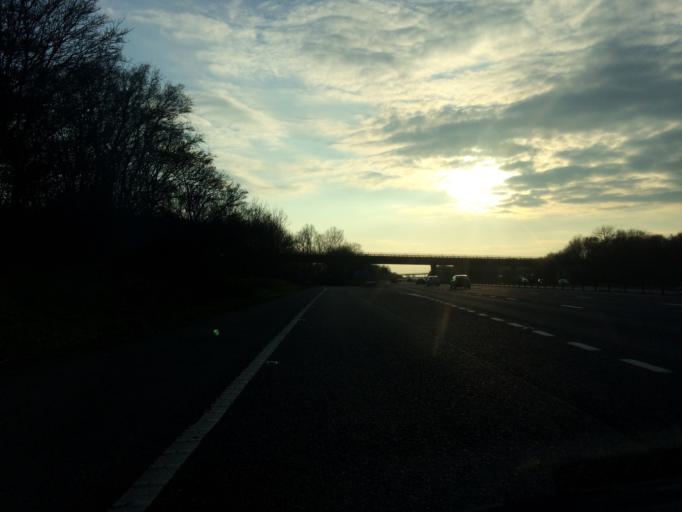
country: GB
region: England
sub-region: Wiltshire
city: Norton
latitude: 51.5112
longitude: -2.1510
